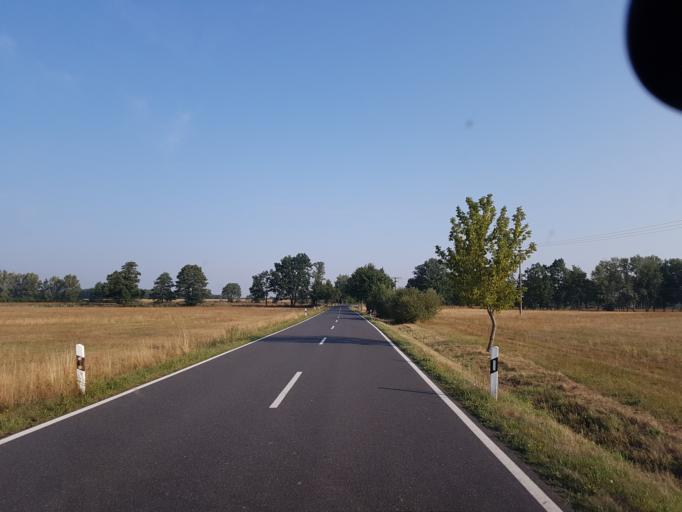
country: DE
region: Brandenburg
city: Finsterwalde
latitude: 51.6540
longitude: 13.7349
